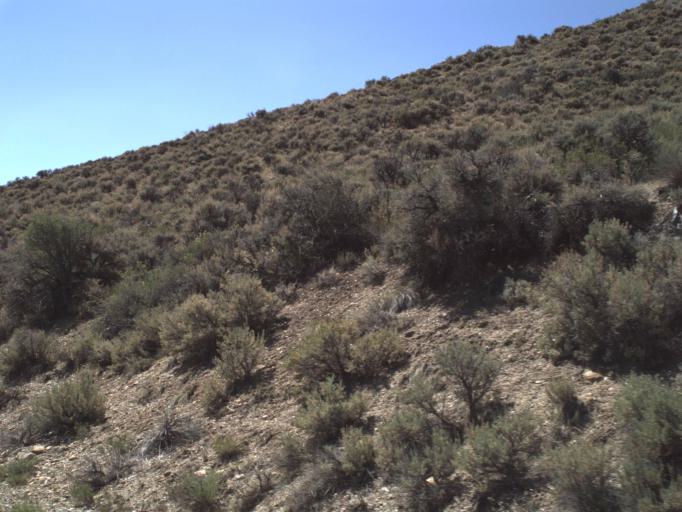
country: US
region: Utah
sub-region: Rich County
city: Randolph
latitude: 41.5005
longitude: -111.3195
